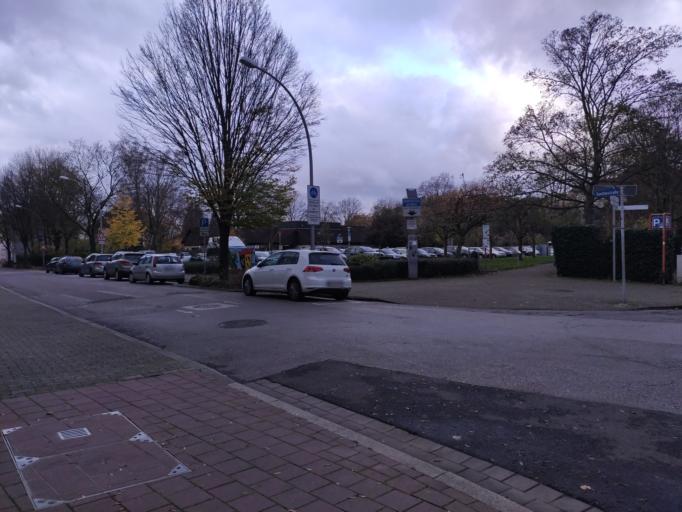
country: DE
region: North Rhine-Westphalia
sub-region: Regierungsbezirk Munster
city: Gladbeck
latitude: 51.5719
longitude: 6.9922
